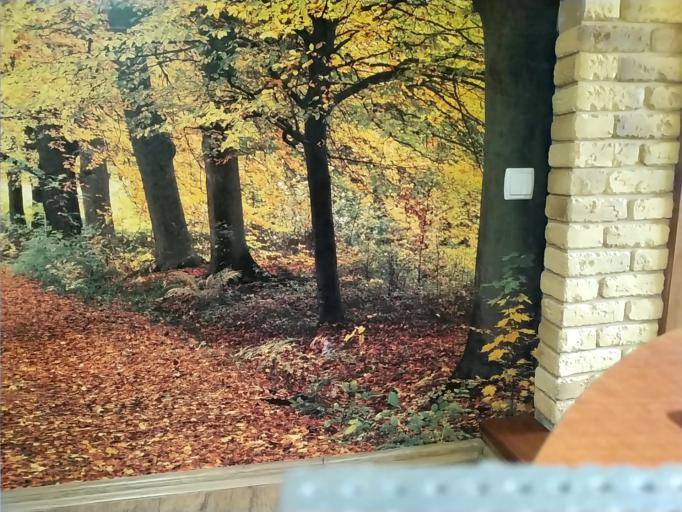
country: RU
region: Tverskaya
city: Kalashnikovo
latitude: 57.2760
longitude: 35.2790
